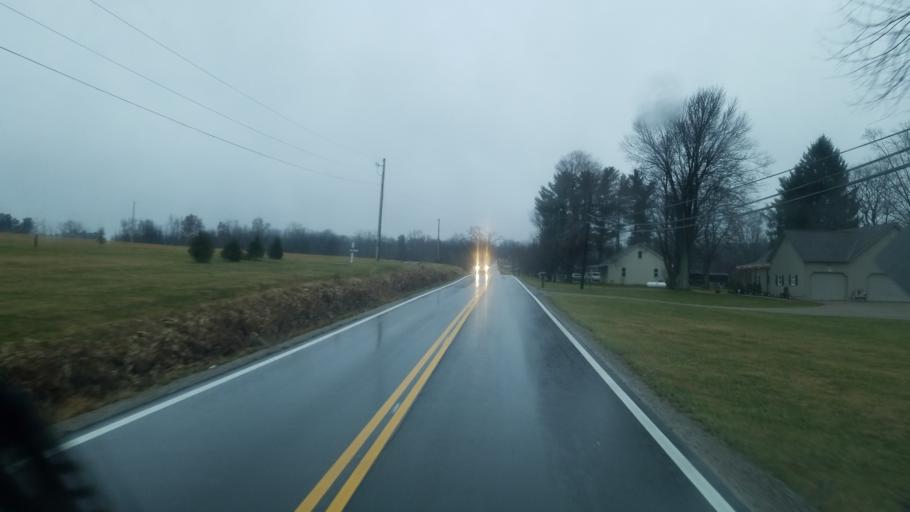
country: US
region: Ohio
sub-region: Licking County
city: Newark
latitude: 40.0756
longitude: -82.3543
